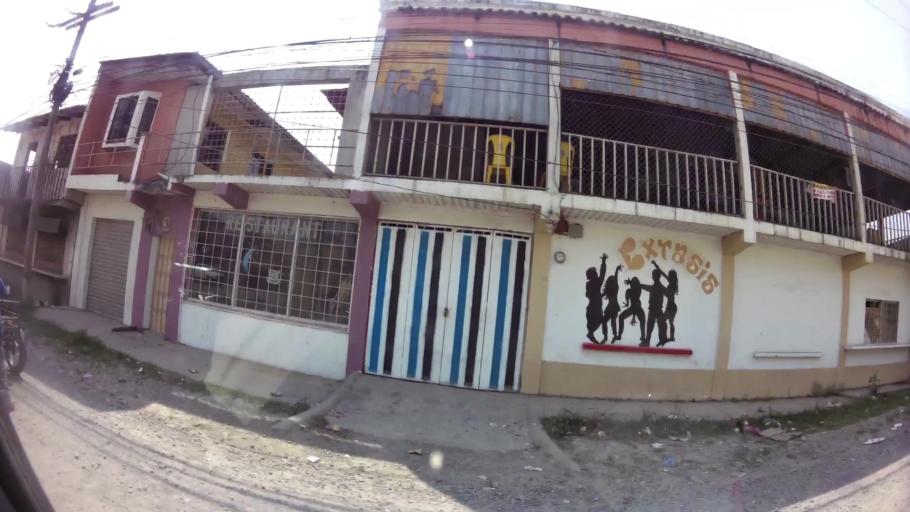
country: HN
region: Comayagua
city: Siguatepeque
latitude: 14.5834
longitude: -87.8458
